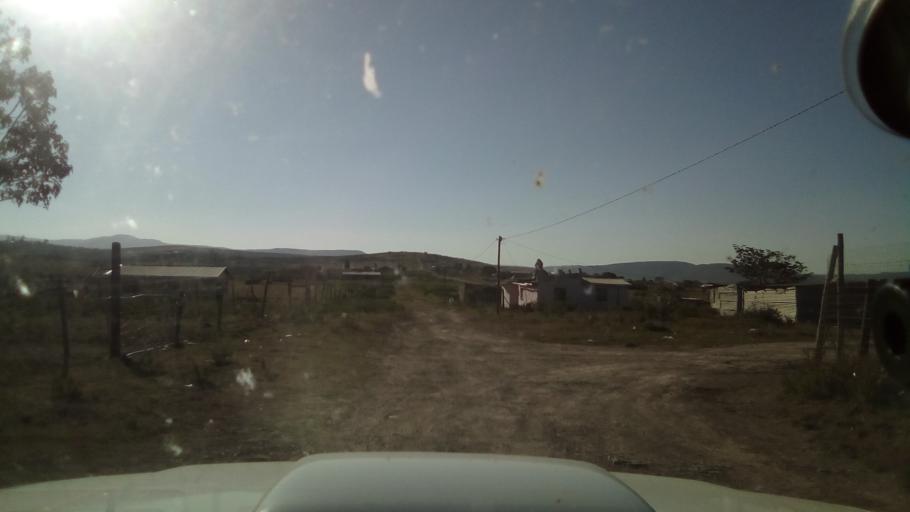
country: ZA
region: Eastern Cape
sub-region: Buffalo City Metropolitan Municipality
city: Bhisho
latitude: -32.8185
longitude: 27.3665
